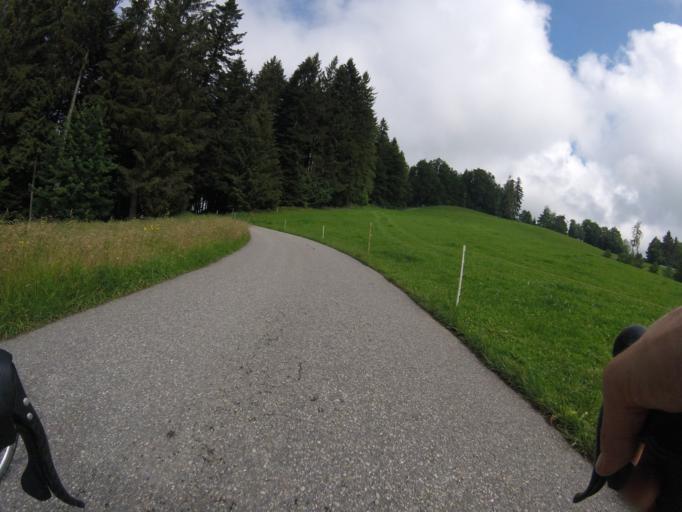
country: CH
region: Bern
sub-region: Bern-Mittelland District
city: Walkringen
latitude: 46.9662
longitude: 7.5983
